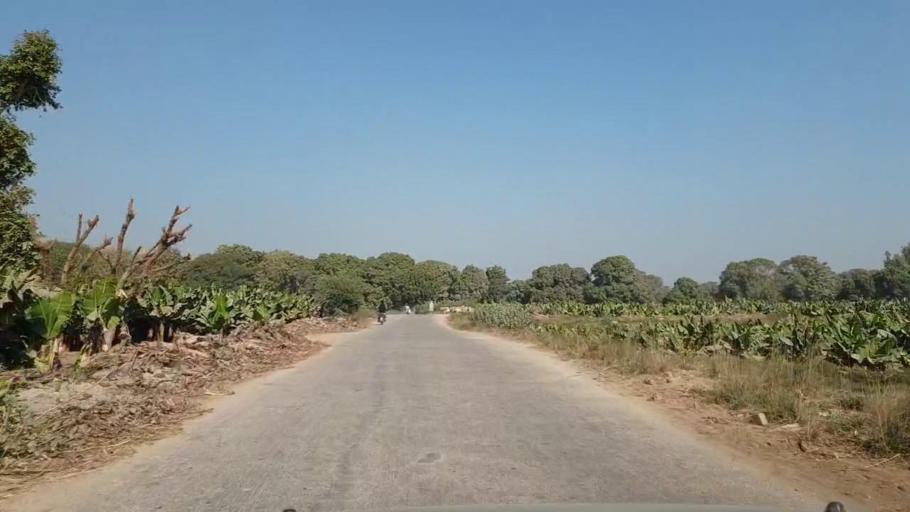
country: PK
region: Sindh
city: Matiari
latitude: 25.6181
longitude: 68.5942
